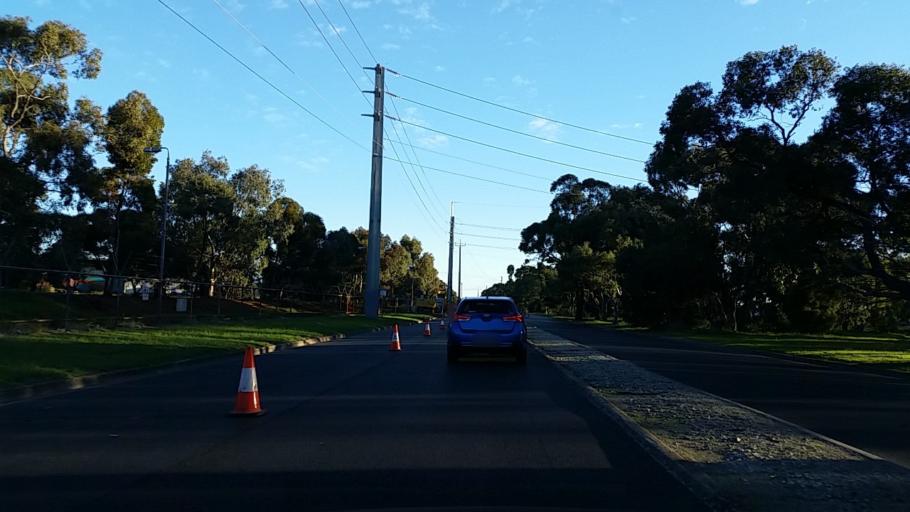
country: AU
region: South Australia
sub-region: Salisbury
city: Salisbury
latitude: -34.7436
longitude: 138.6487
